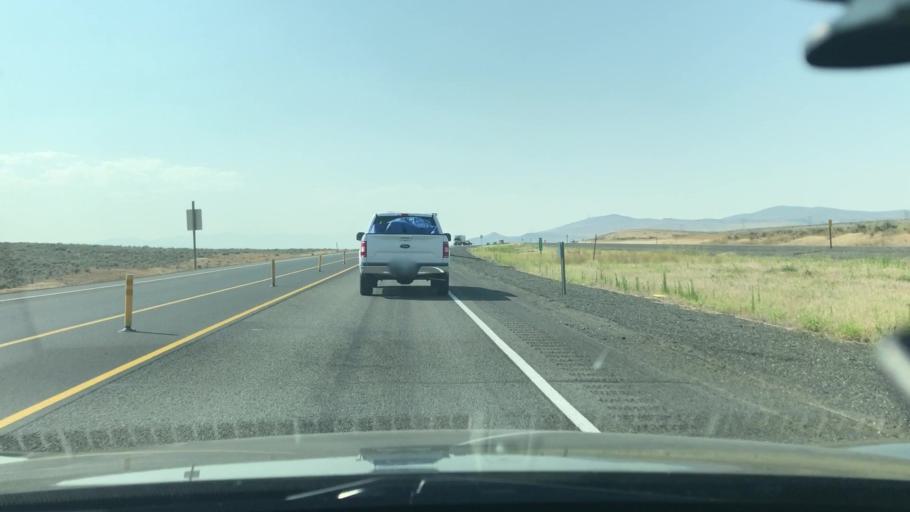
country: US
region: Oregon
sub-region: Baker County
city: Baker City
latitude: 44.6895
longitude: -117.6835
